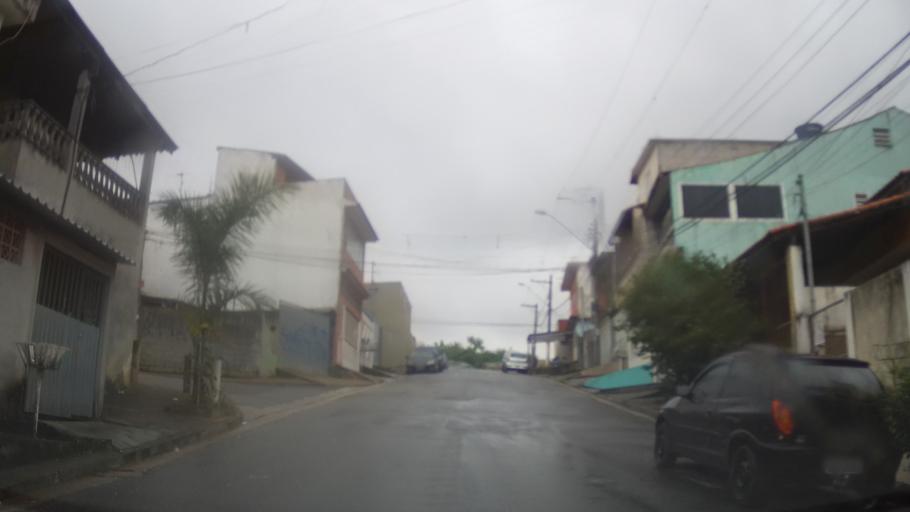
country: BR
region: Sao Paulo
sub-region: Guarulhos
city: Guarulhos
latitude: -23.4379
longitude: -46.5326
